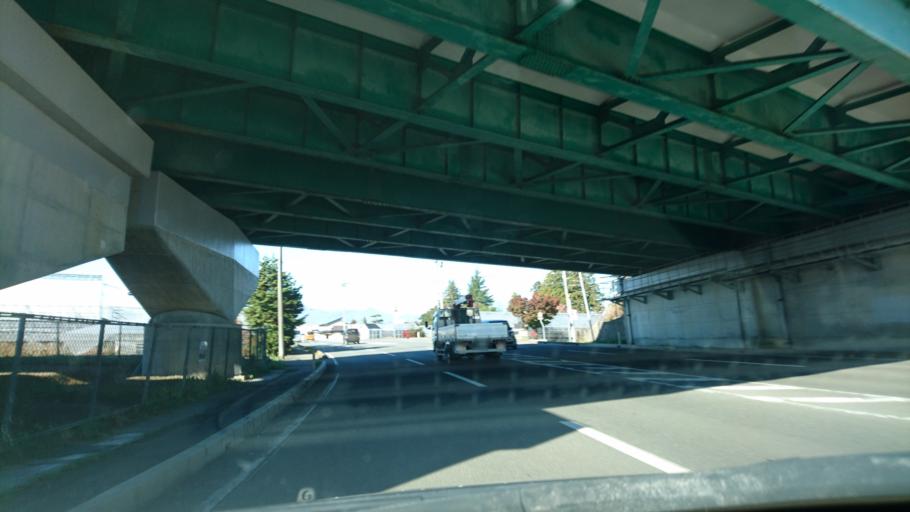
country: JP
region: Iwate
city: Mizusawa
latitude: 39.1444
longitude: 141.1200
